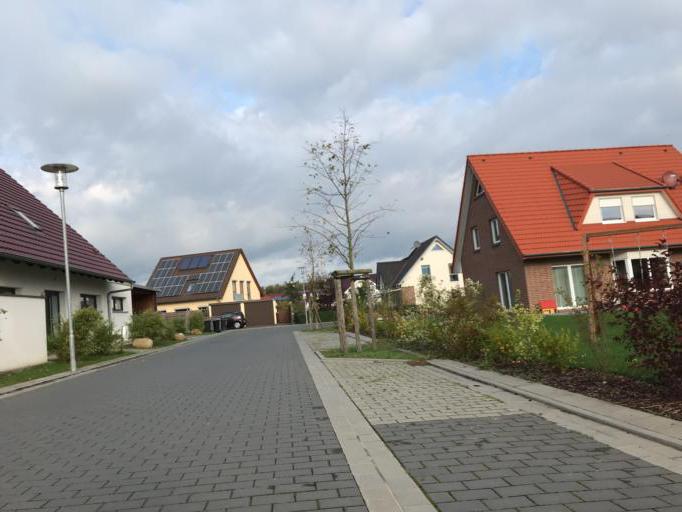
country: DE
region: Lower Saxony
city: Braunschweig
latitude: 52.2878
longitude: 10.4677
